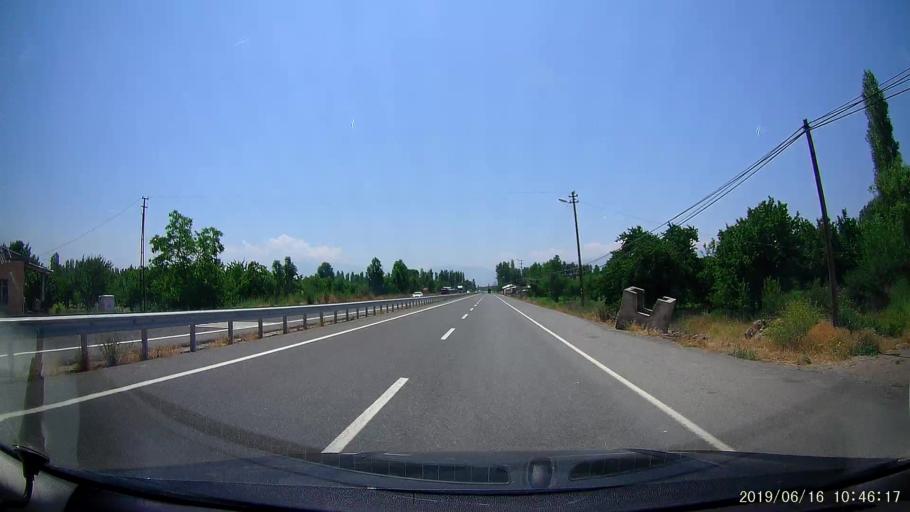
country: AM
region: Armavir
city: Shenavan
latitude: 40.0232
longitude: 43.8783
